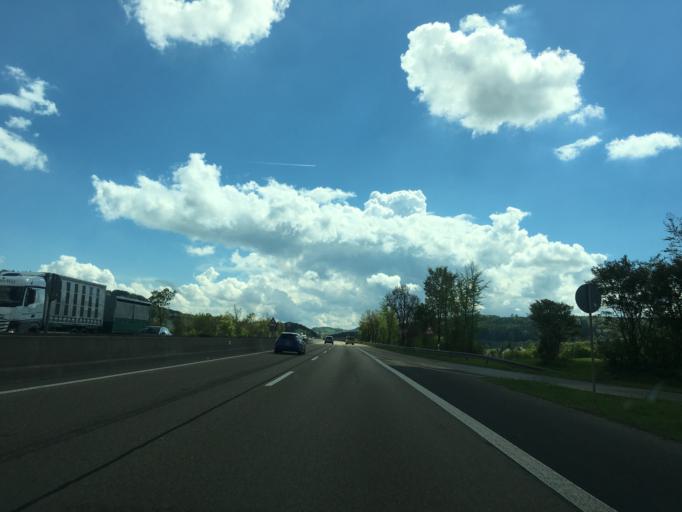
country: DE
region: Bavaria
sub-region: Regierungsbezirk Unterfranken
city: Motten
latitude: 50.4171
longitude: 9.7347
